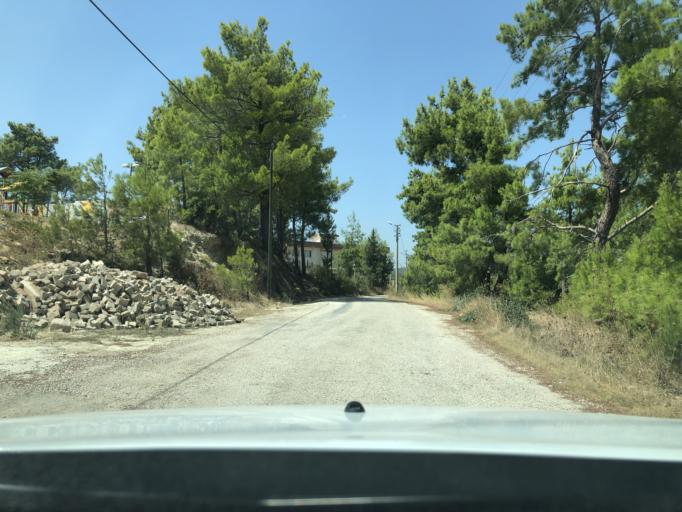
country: TR
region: Antalya
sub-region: Manavgat
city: Kizilagac
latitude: 36.8583
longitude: 31.5542
